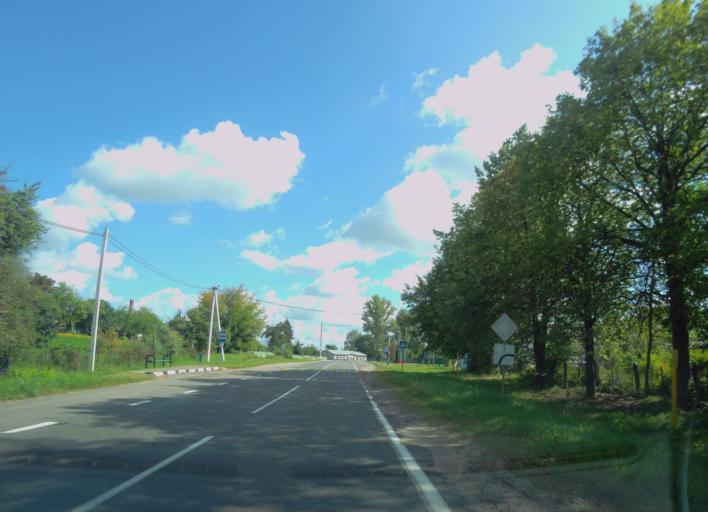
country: BY
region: Minsk
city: Zyembin
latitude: 54.3607
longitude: 28.3408
